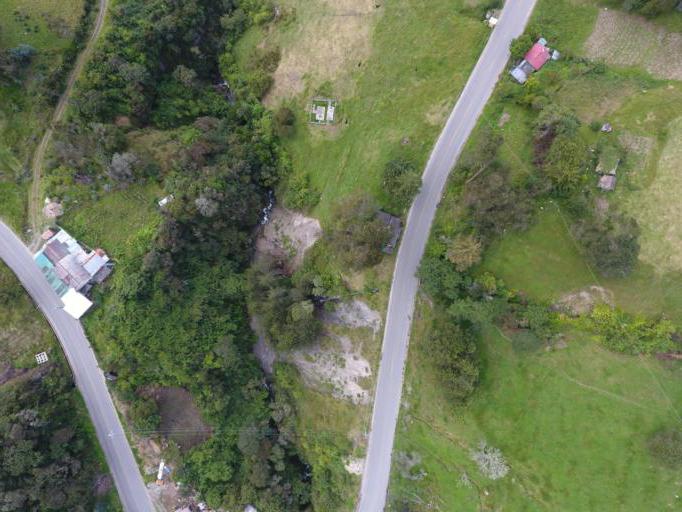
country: EC
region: Canar
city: Azogues
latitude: -2.6391
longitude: -78.5989
